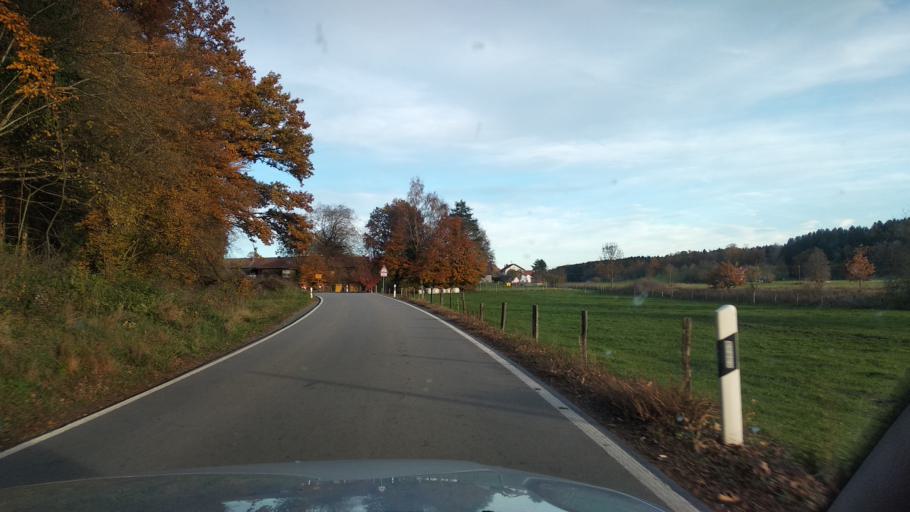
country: DE
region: Bavaria
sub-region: Upper Bavaria
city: Bruck
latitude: 48.0398
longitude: 11.9203
